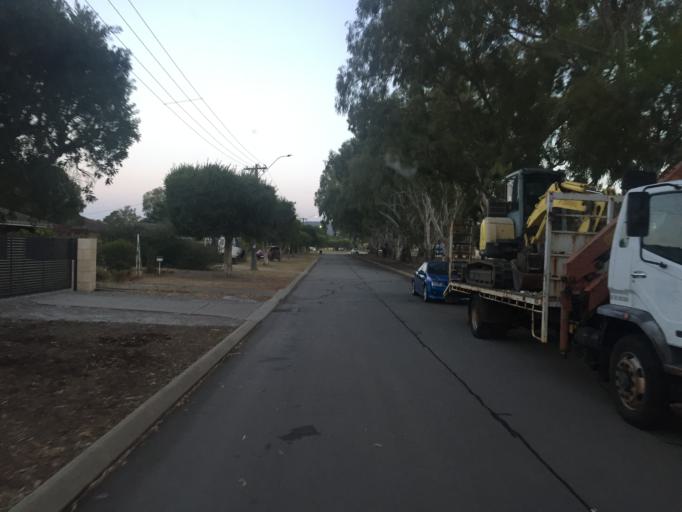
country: AU
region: Western Australia
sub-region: Gosnells
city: Maddington
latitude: -32.0306
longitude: 115.9874
